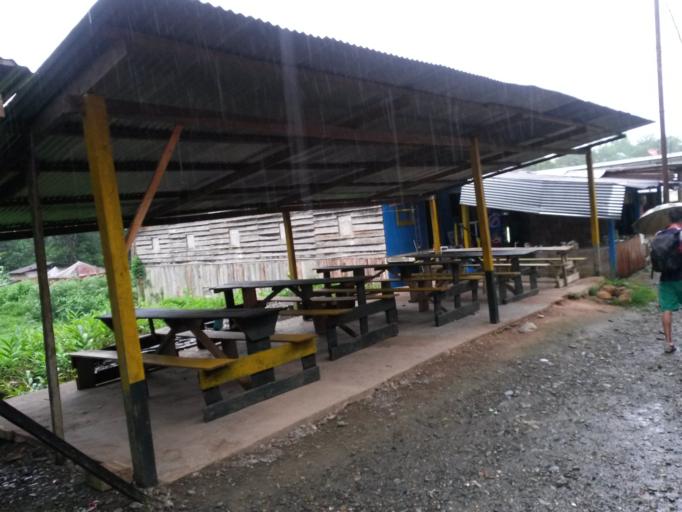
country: CO
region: Valle del Cauca
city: Buenaventura
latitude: 3.8371
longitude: -76.8966
